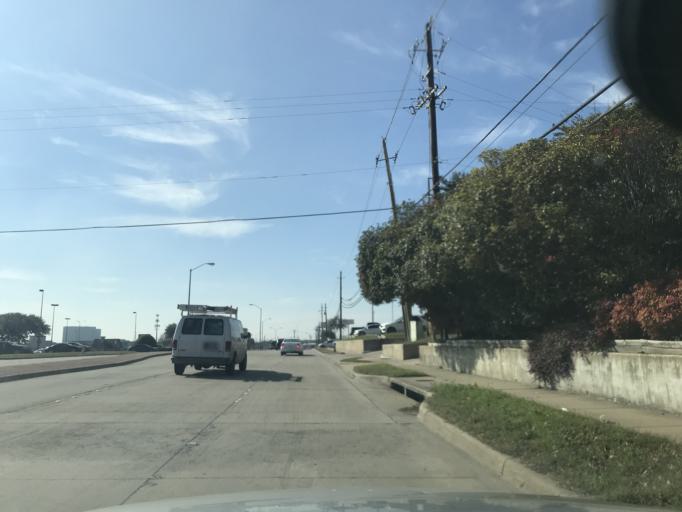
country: US
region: Texas
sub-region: Collin County
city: Plano
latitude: 33.0386
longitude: -96.6952
